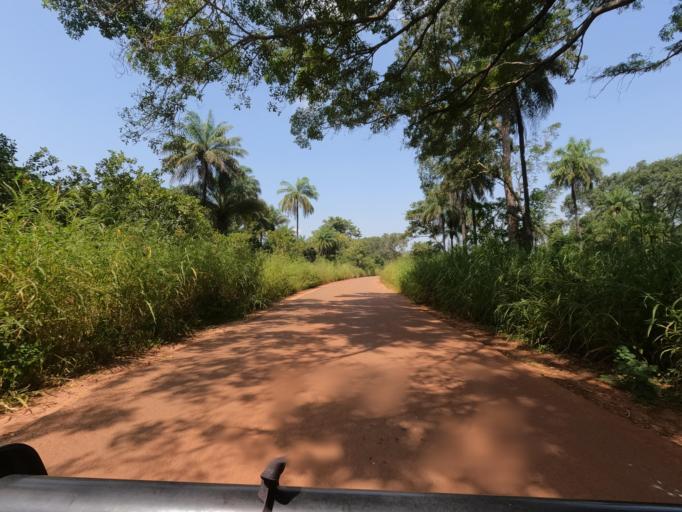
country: GW
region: Oio
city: Bissora
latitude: 12.3589
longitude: -15.7716
